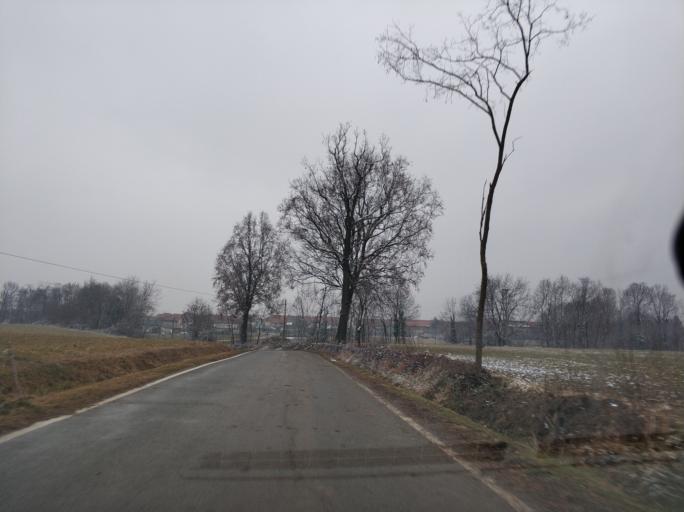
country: IT
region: Piedmont
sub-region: Provincia di Torino
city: San Francesco al Campo
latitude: 45.2318
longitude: 7.6607
